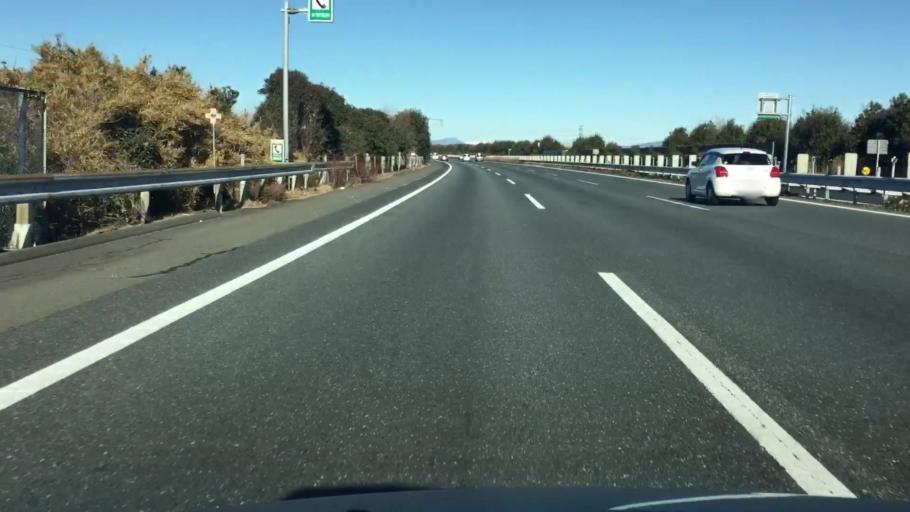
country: JP
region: Saitama
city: Honjo
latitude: 36.1915
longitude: 139.1891
